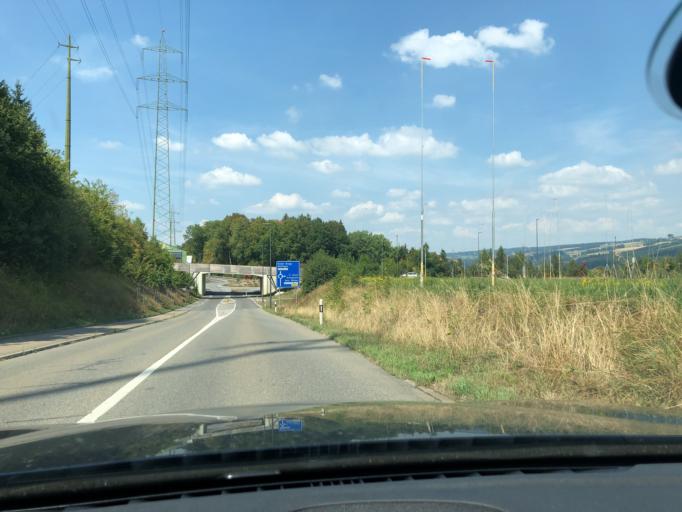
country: CH
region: Aargau
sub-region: Bezirk Bremgarten
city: Bremgarten
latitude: 47.3543
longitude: 8.3248
